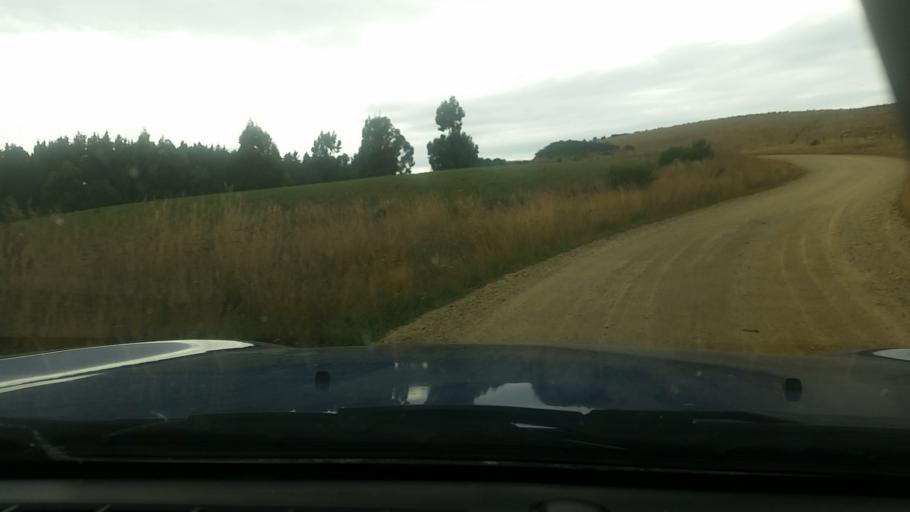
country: NZ
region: Otago
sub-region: Clutha District
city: Balclutha
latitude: -45.7022
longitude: 169.4777
